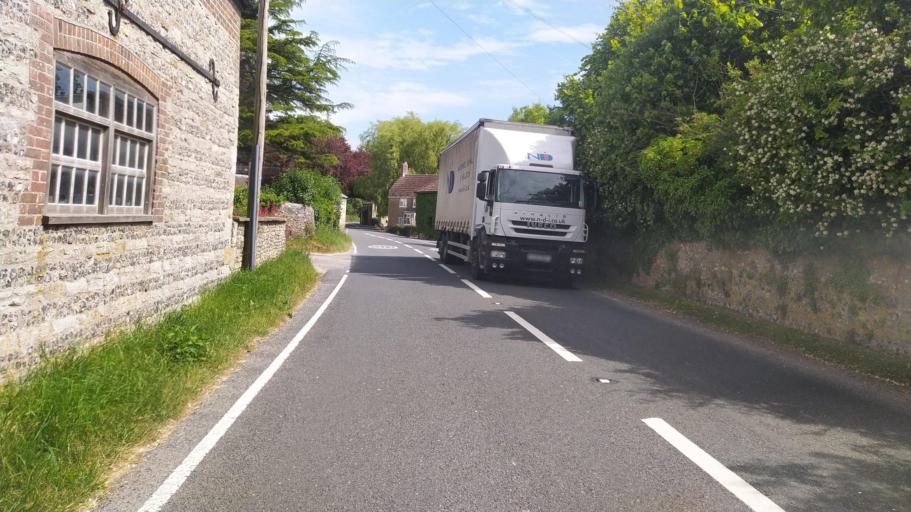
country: GB
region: England
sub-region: Dorset
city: Dorchester
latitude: 50.7739
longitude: -2.4740
